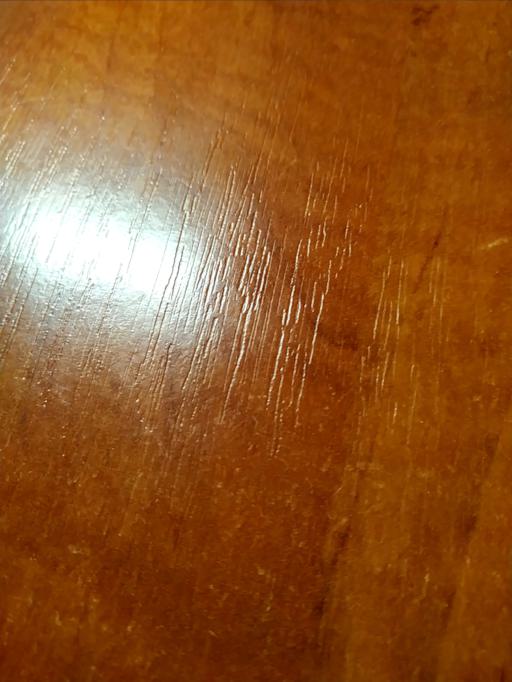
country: RU
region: Kaluga
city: Iznoski
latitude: 54.9764
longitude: 35.4129
